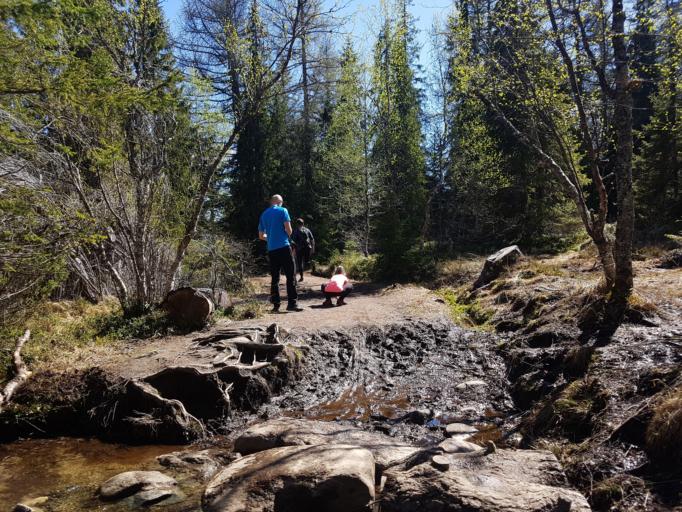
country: NO
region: Sor-Trondelag
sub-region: Trondheim
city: Trondheim
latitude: 63.4283
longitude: 10.3133
